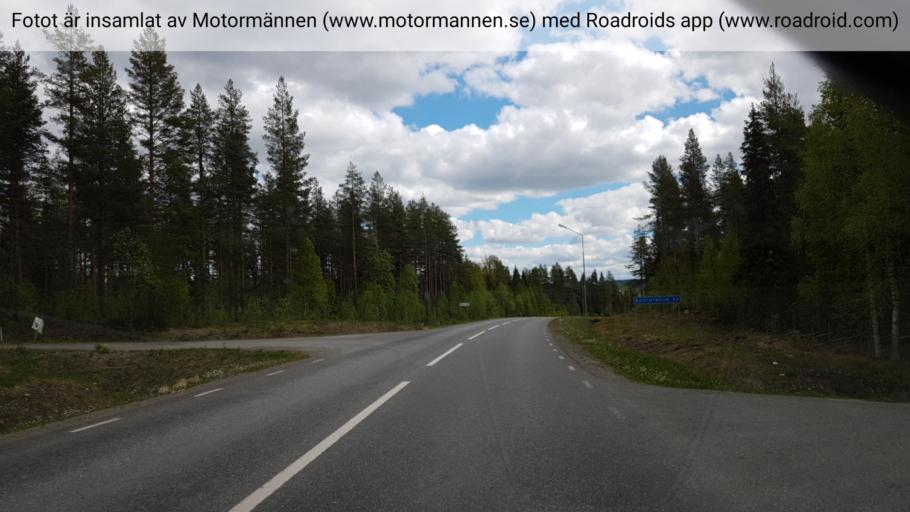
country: SE
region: Vaesterbotten
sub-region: Norsjo Kommun
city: Norsjoe
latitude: 64.9107
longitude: 19.5103
